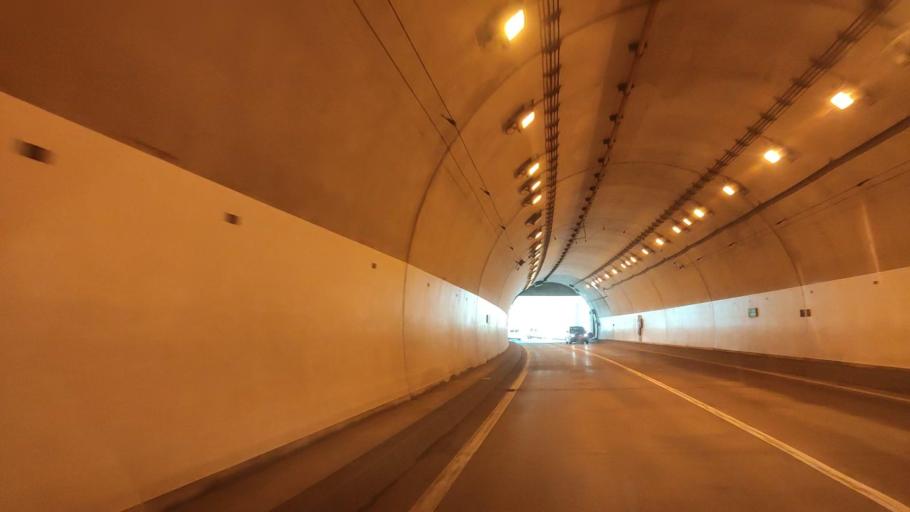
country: JP
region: Hokkaido
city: Rumoi
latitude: 43.6739
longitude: 141.3469
